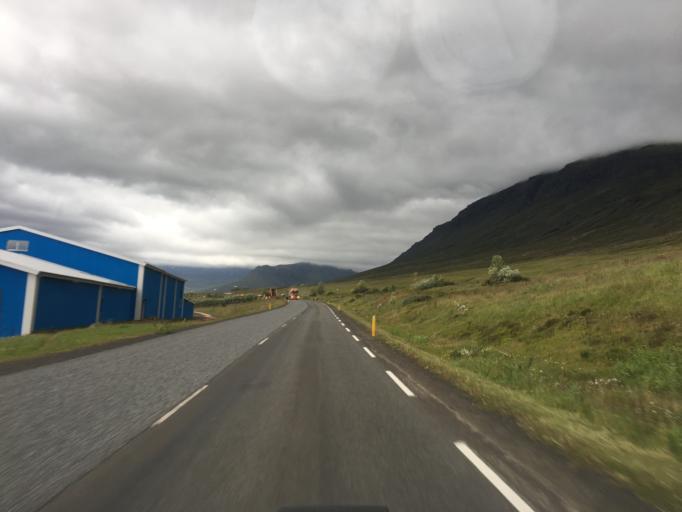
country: IS
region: East
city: Neskaupstadur
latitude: 65.1460
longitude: -13.7249
